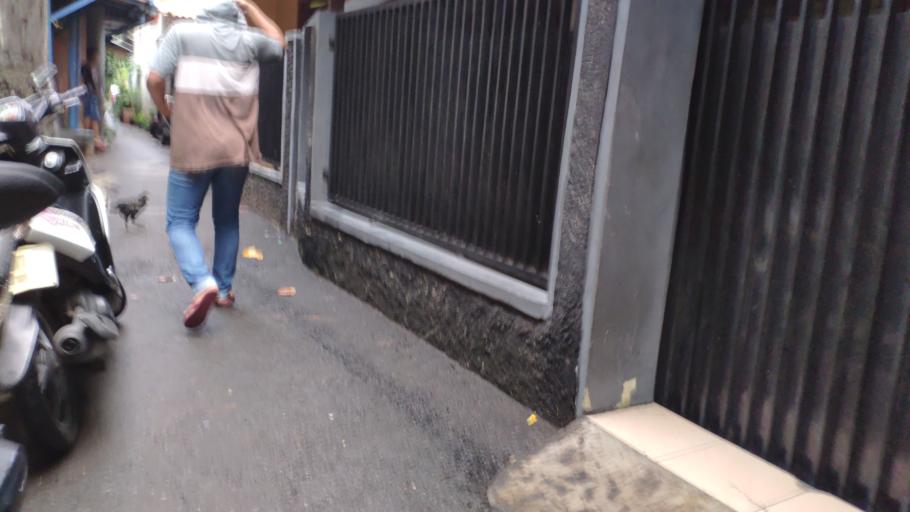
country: ID
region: Jakarta Raya
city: Jakarta
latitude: -6.2073
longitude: 106.8733
